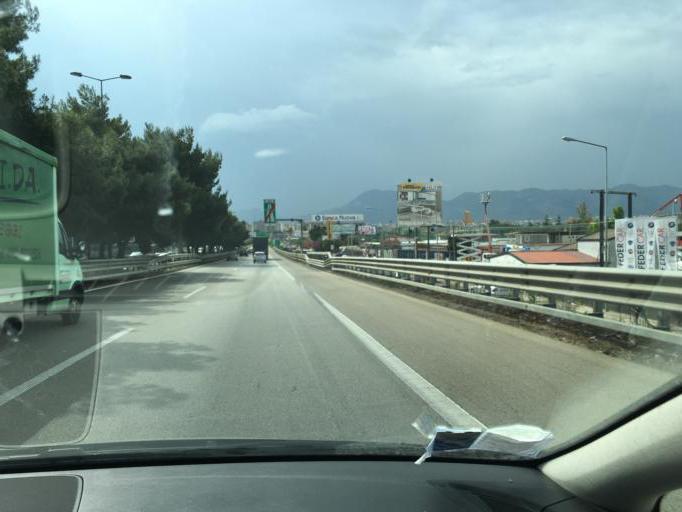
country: IT
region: Sicily
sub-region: Palermo
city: Palermo
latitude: 38.1540
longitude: 13.3197
